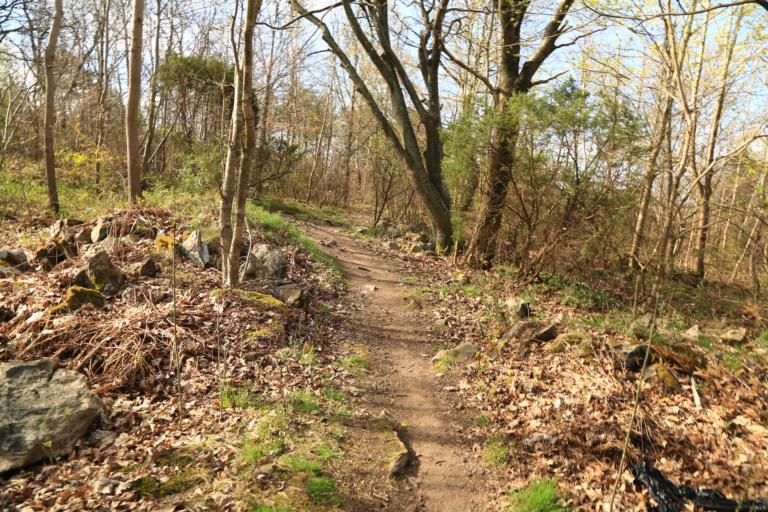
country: SE
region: Halland
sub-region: Varbergs Kommun
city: Varberg
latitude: 57.1006
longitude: 12.2800
